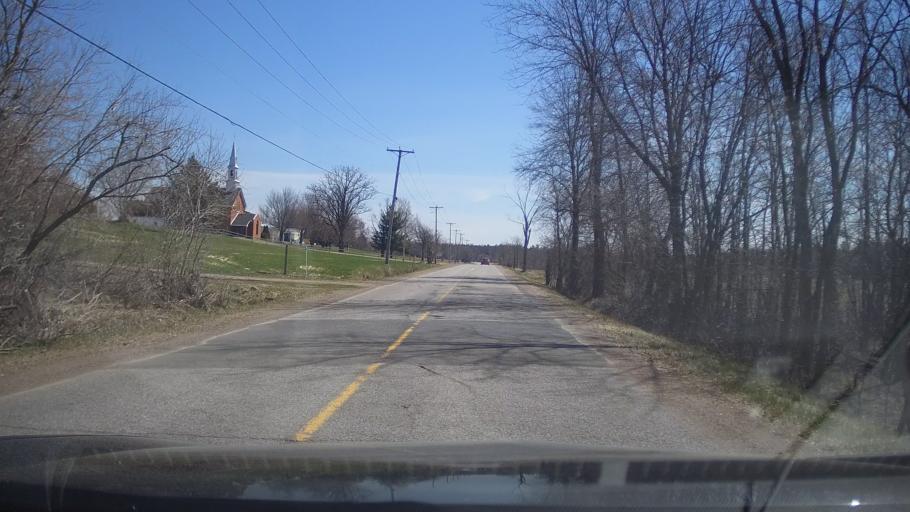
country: CA
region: Ontario
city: Arnprior
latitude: 45.5315
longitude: -76.3784
